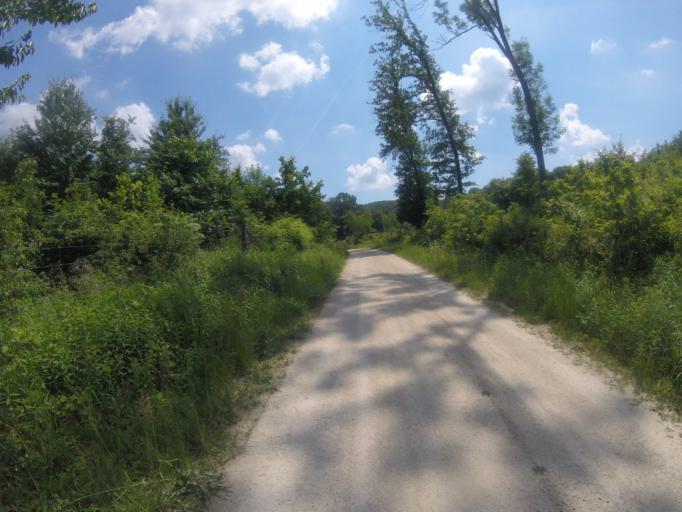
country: HU
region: Veszprem
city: Cseteny
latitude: 47.2670
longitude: 17.9987
